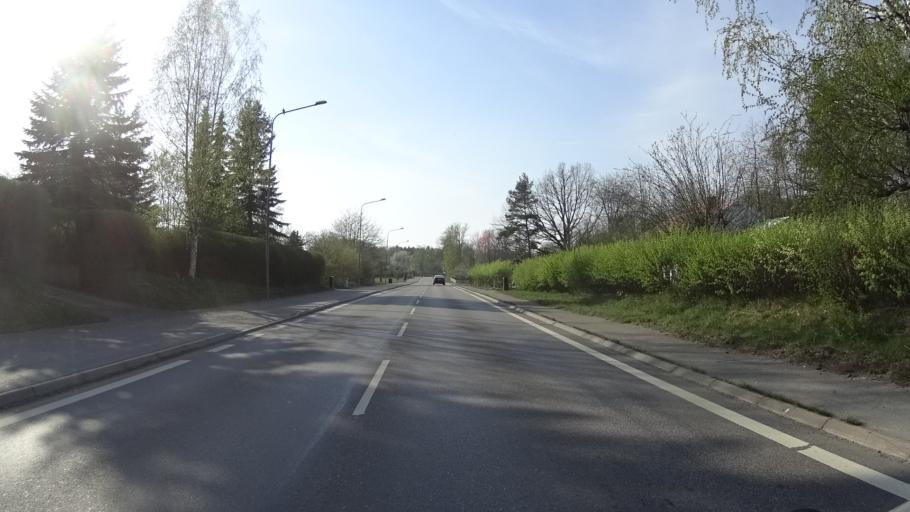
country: SE
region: Vaestra Goetaland
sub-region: Gotene Kommun
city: Goetene
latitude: 58.6297
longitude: 13.4460
